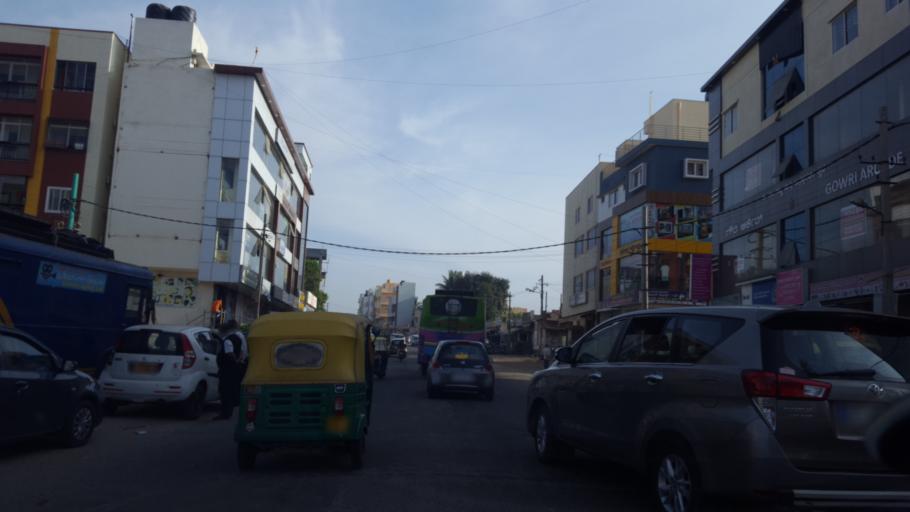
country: IN
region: Karnataka
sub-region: Bangalore Urban
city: Bangalore
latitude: 12.9200
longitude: 77.5139
